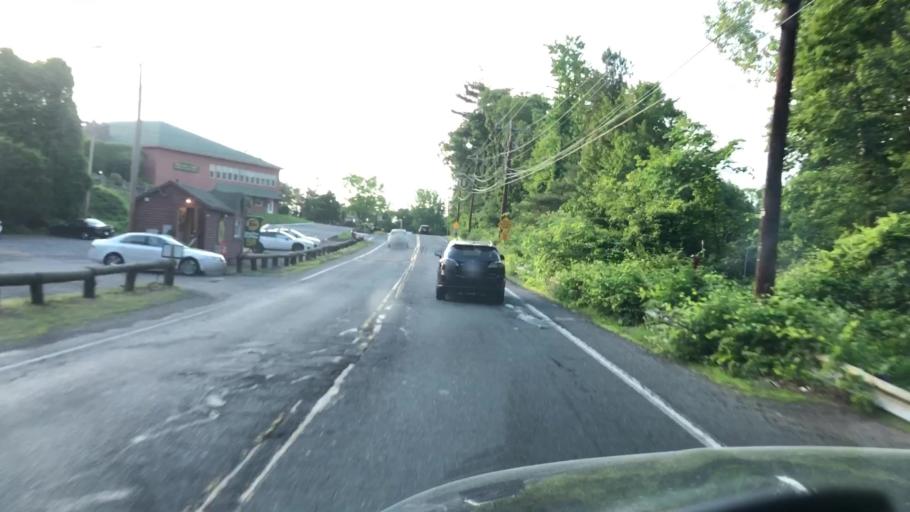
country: US
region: Massachusetts
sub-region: Hampshire County
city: Easthampton
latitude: 42.2359
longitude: -72.6509
